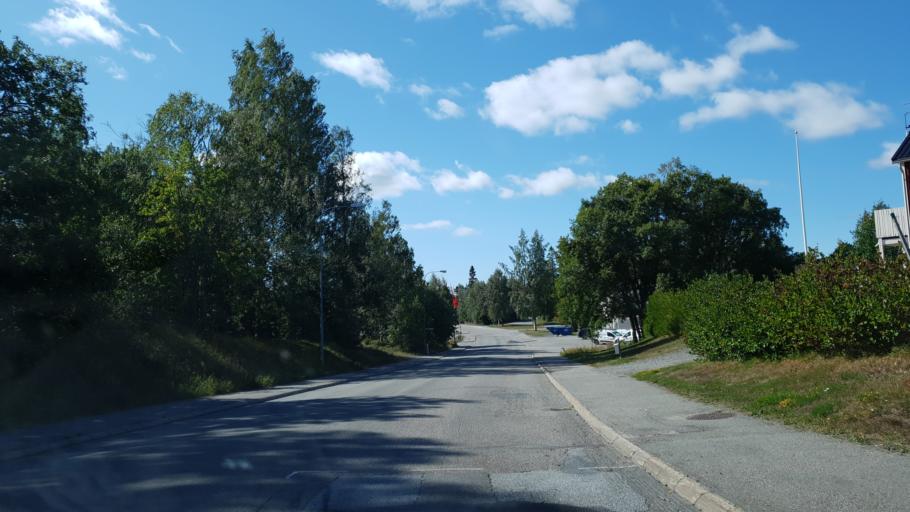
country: SE
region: Vaesterbotten
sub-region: Umea Kommun
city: Holmsund
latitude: 63.7119
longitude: 20.3748
